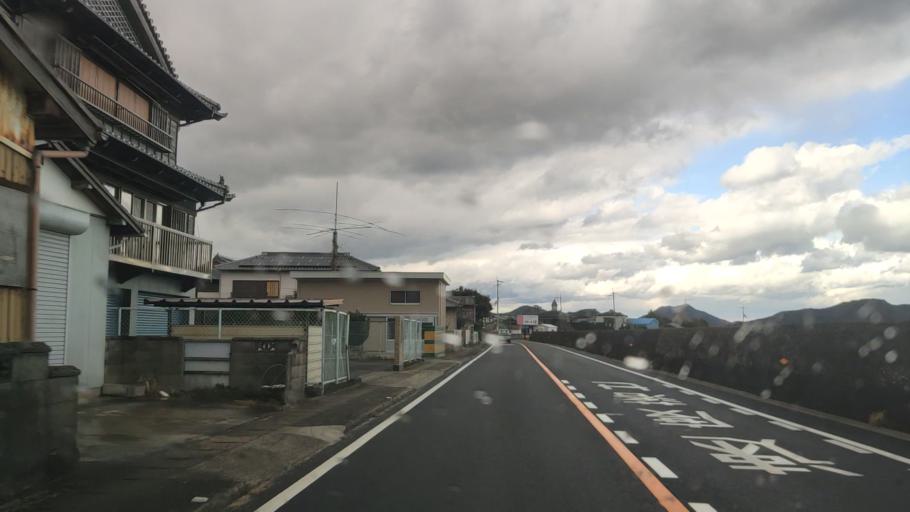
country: JP
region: Tokushima
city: Ishii
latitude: 34.2184
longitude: 134.4163
